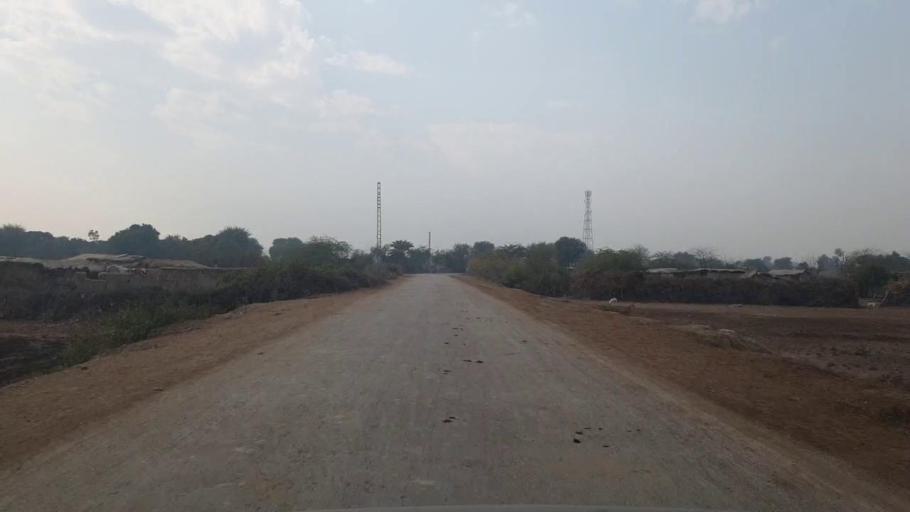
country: PK
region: Sindh
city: Hala
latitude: 25.8962
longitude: 68.4082
